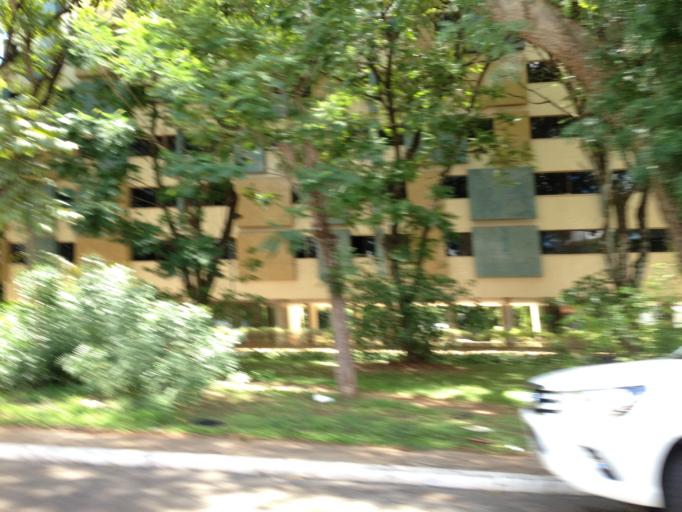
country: BR
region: Federal District
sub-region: Brasilia
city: Brasilia
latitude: -15.8188
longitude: -47.9139
